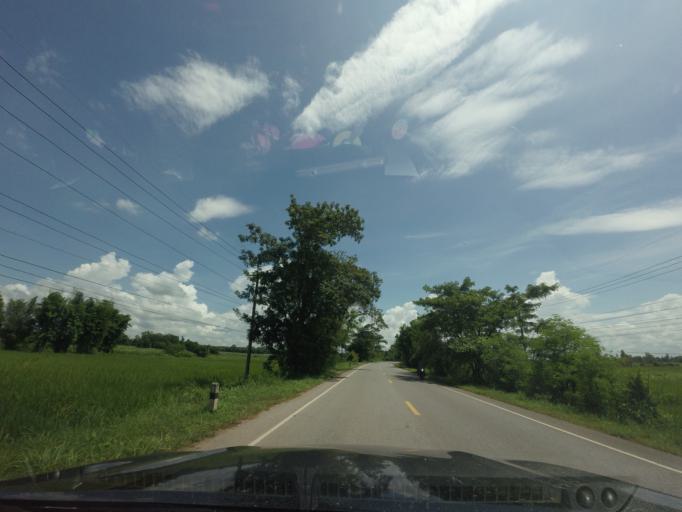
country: TH
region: Changwat Udon Thani
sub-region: Amphoe Ban Phue
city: Ban Phue
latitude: 17.7184
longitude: 102.3952
